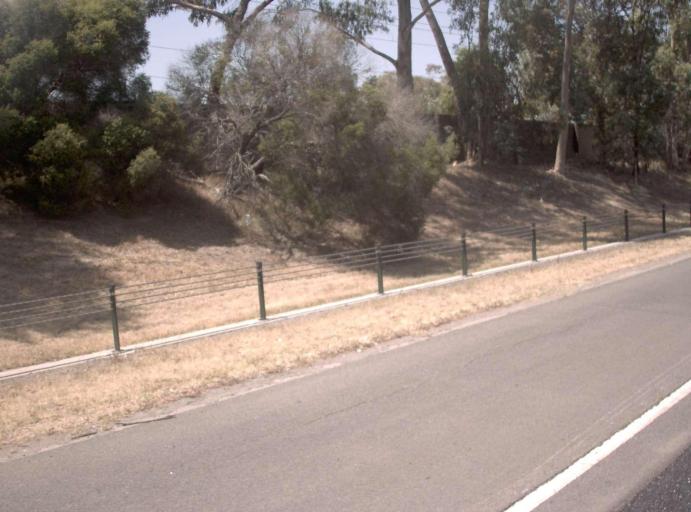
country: AU
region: Victoria
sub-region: Boroondara
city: Balwyn North
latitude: -37.7823
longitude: 145.0993
